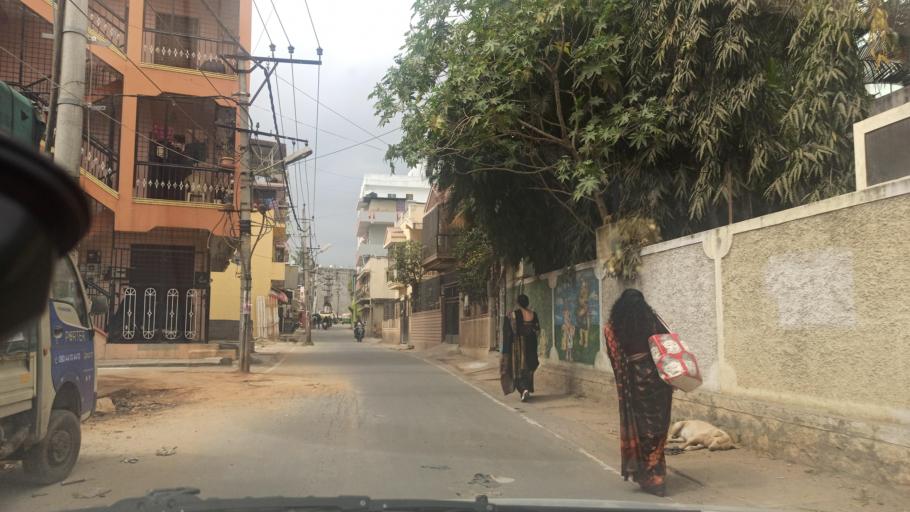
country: IN
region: Karnataka
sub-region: Bangalore Urban
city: Bangalore
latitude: 13.0356
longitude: 77.5982
